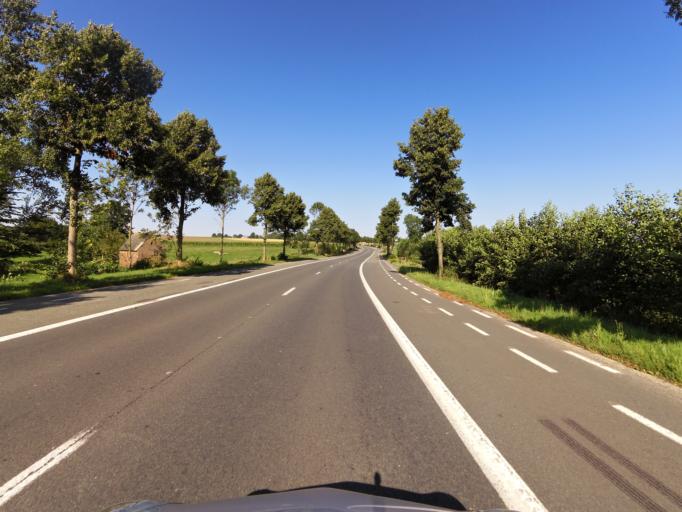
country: BE
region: Wallonia
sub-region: Province du Hainaut
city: Flobecq
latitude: 50.8185
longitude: 3.7164
